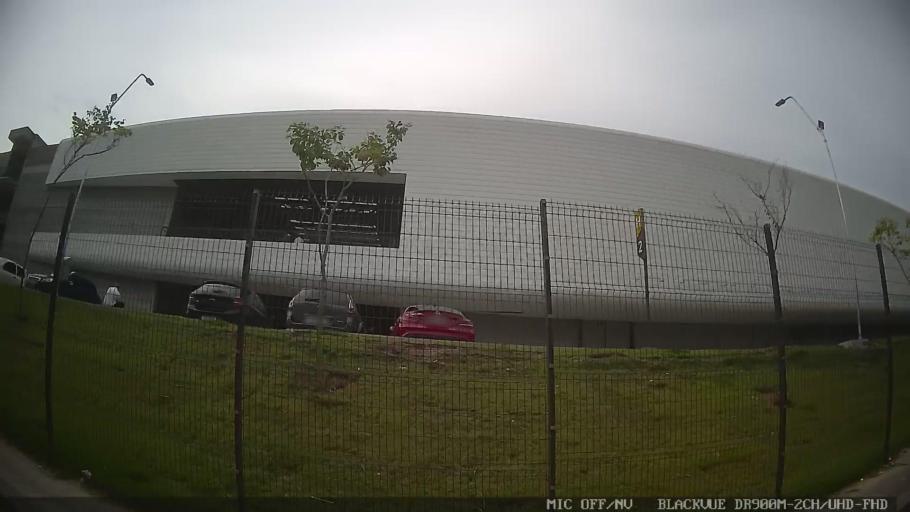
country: BR
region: Sao Paulo
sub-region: Aruja
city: Aruja
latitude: -23.4333
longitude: -46.2729
